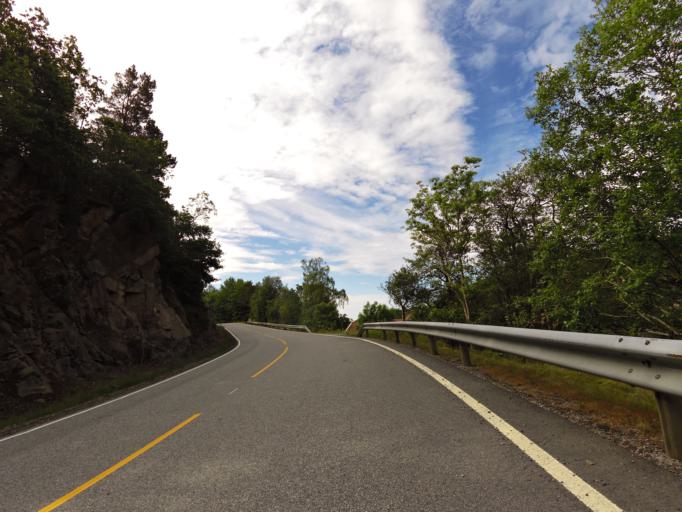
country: NO
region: Vest-Agder
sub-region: Lindesnes
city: Vigeland
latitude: 58.0571
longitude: 7.1809
